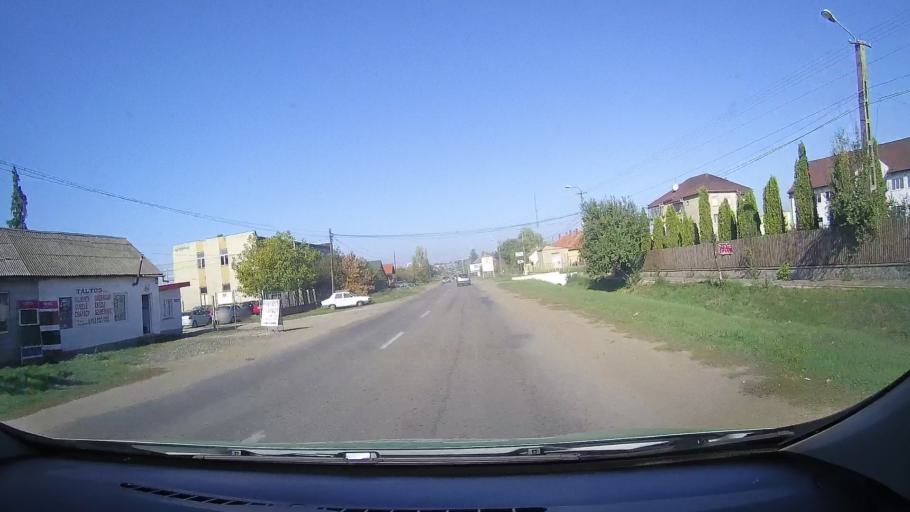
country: RO
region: Satu Mare
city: Carei
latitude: 47.6747
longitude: 22.4803
